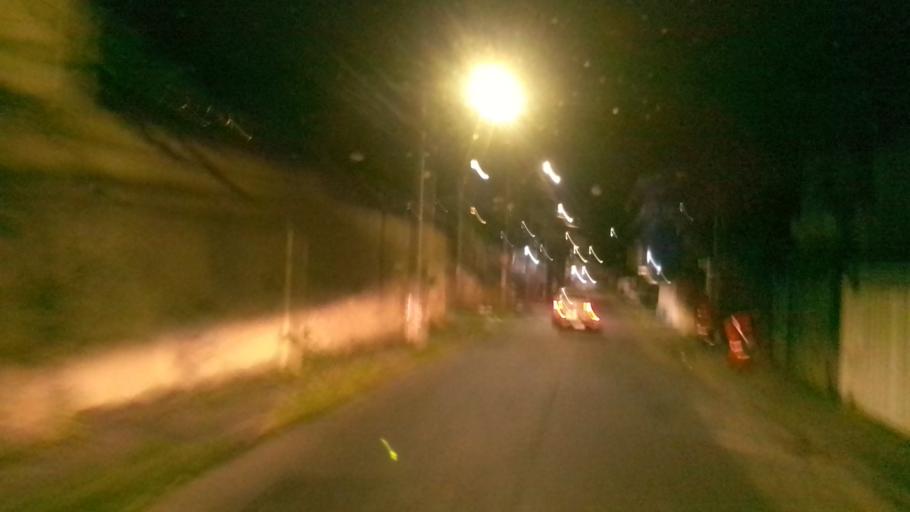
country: BR
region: Minas Gerais
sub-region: Belo Horizonte
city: Belo Horizonte
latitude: -19.9066
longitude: -43.9600
